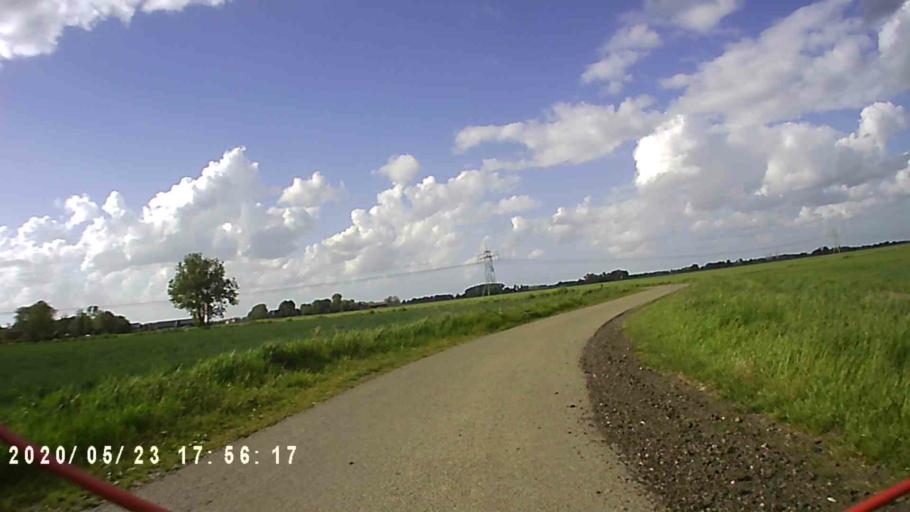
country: NL
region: Groningen
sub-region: Gemeente Slochteren
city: Slochteren
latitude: 53.2502
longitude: 6.7451
